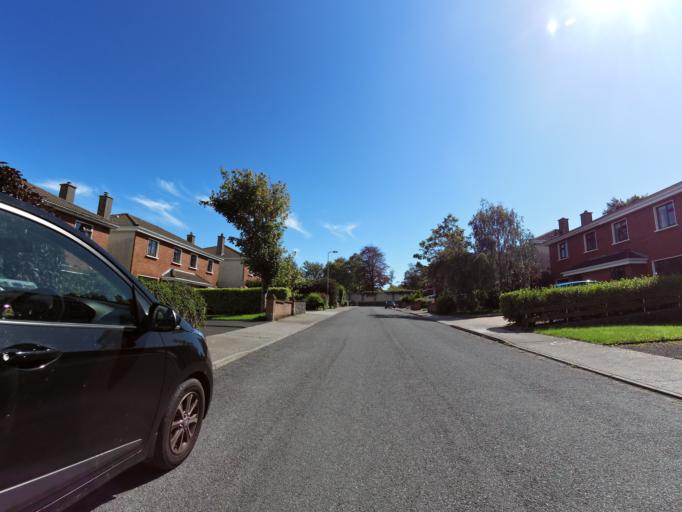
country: IE
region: Connaught
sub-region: County Galway
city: Gaillimh
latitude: 53.2892
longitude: -9.0820
